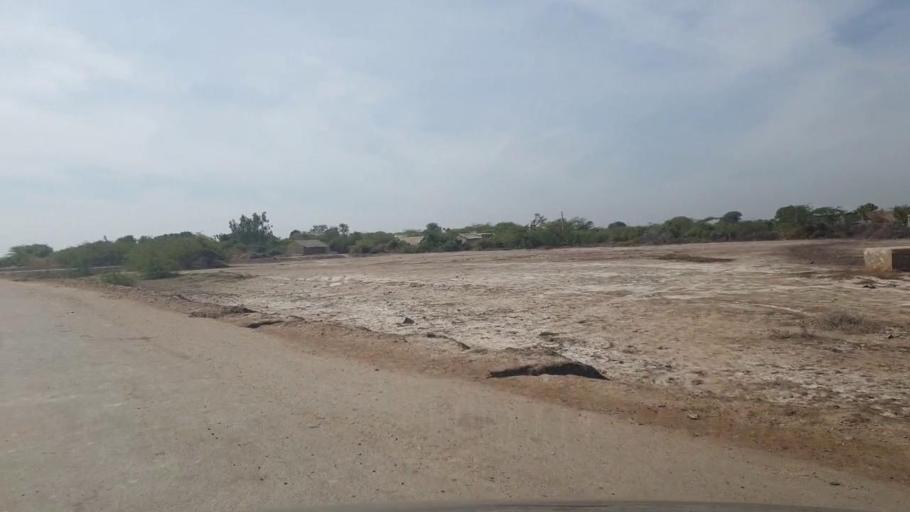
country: PK
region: Sindh
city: Umarkot
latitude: 25.3312
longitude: 69.5937
